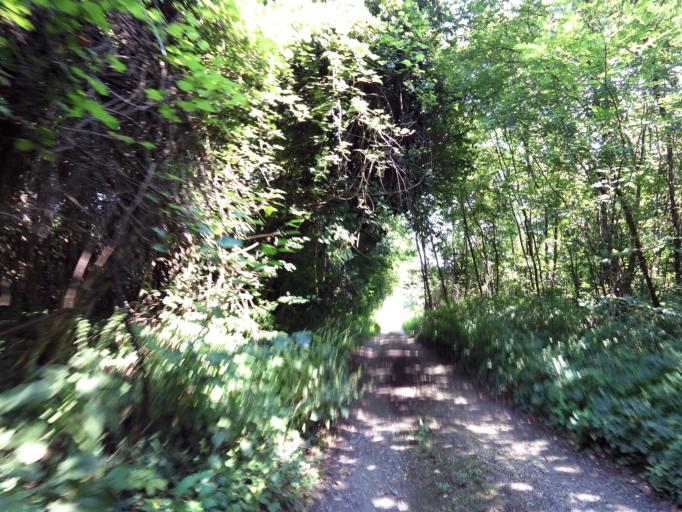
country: HU
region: Zala
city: Vonyarcvashegy
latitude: 46.8318
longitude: 17.3580
